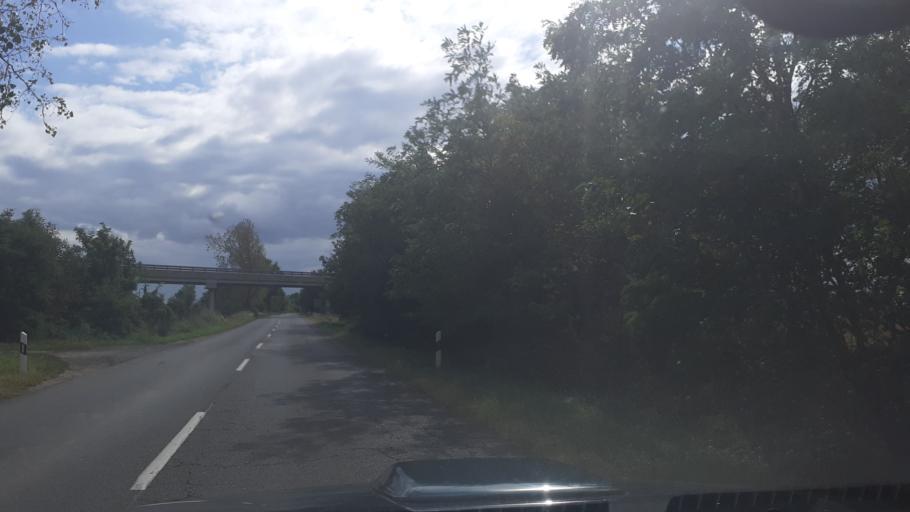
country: HU
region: Bacs-Kiskun
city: Apostag
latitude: 46.8753
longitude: 18.9788
